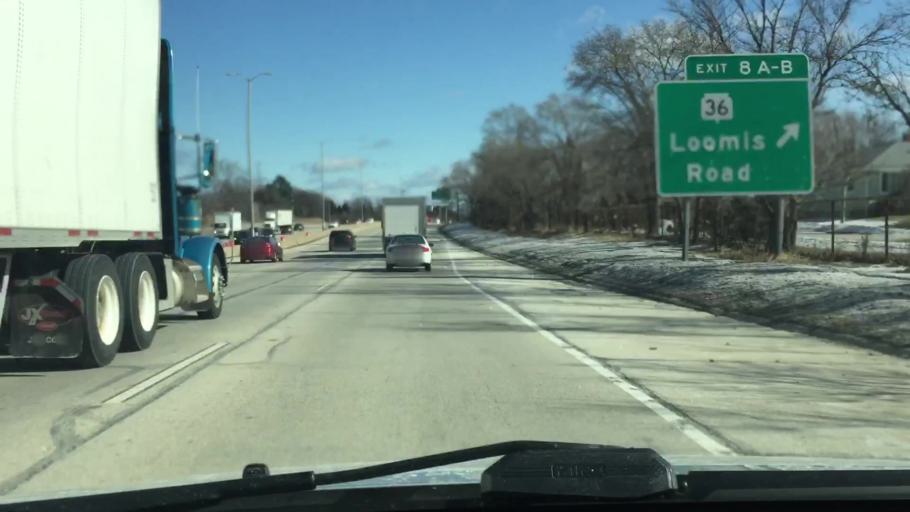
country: US
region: Wisconsin
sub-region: Milwaukee County
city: Greendale
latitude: 42.9624
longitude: -87.9763
